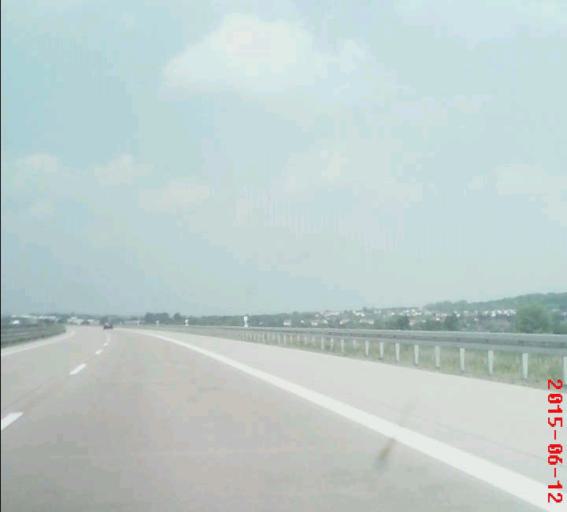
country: DE
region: Thuringia
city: Reinsdorf
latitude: 51.3517
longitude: 11.2682
